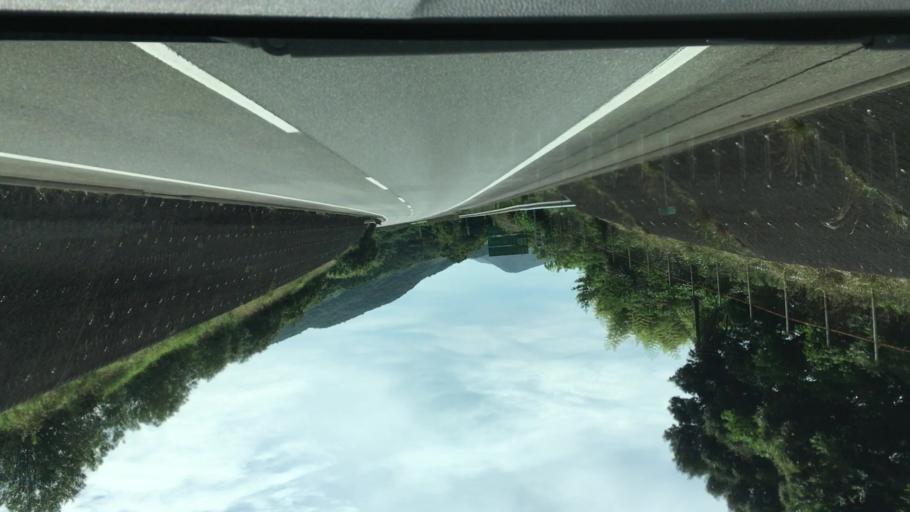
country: JP
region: Yamaguchi
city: Hofu
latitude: 34.0593
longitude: 131.6502
